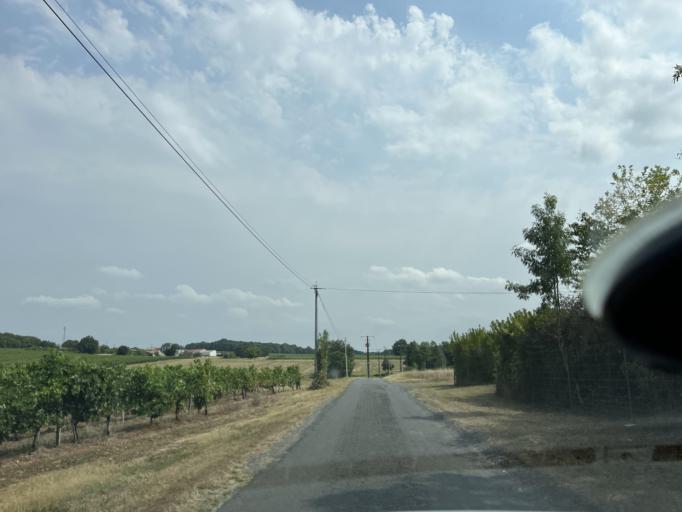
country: FR
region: Poitou-Charentes
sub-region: Departement de la Charente-Maritime
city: Pons
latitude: 45.5951
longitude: -0.5800
